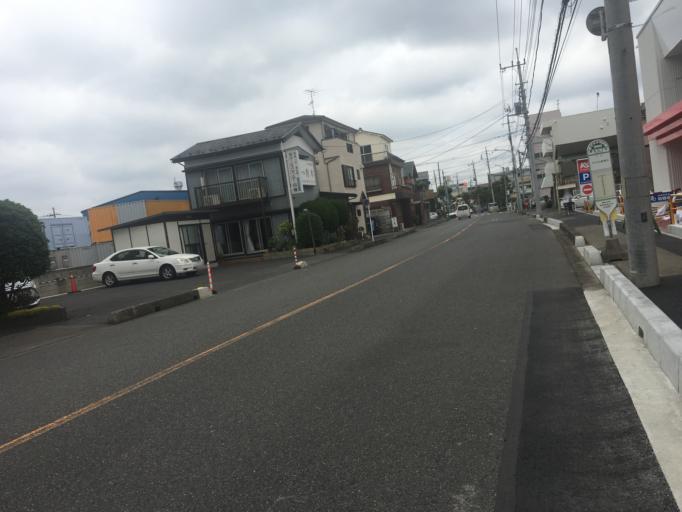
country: JP
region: Saitama
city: Kawaguchi
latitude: 35.8108
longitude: 139.7277
